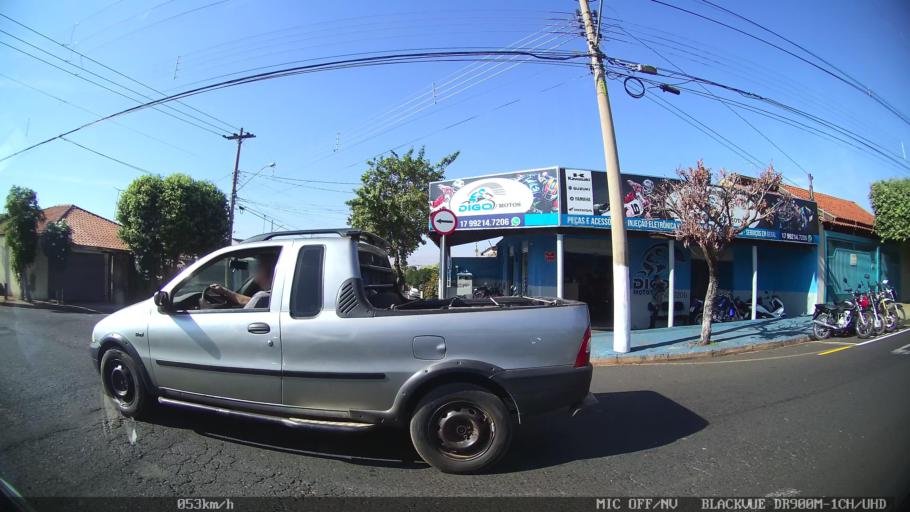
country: BR
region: Sao Paulo
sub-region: Sao Jose Do Rio Preto
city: Sao Jose do Rio Preto
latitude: -20.7784
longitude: -49.4016
